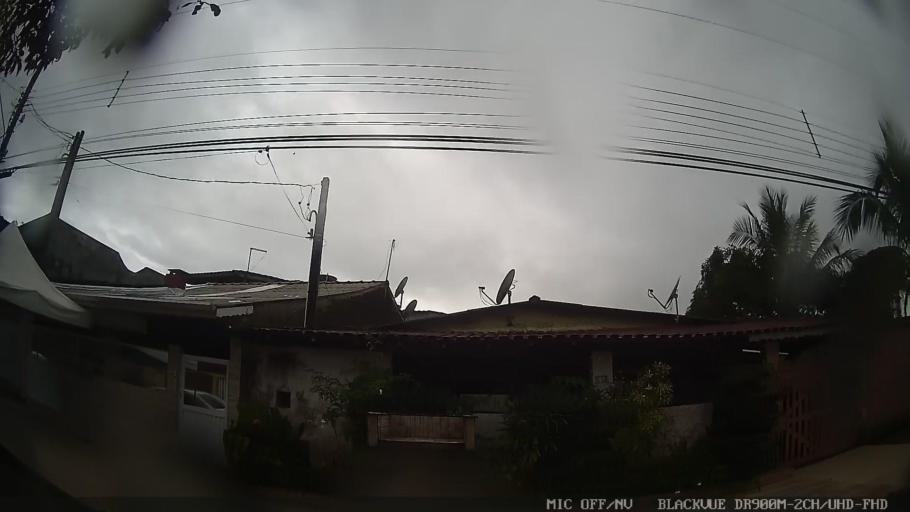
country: BR
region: Sao Paulo
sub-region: Itanhaem
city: Itanhaem
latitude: -24.2320
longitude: -46.8818
